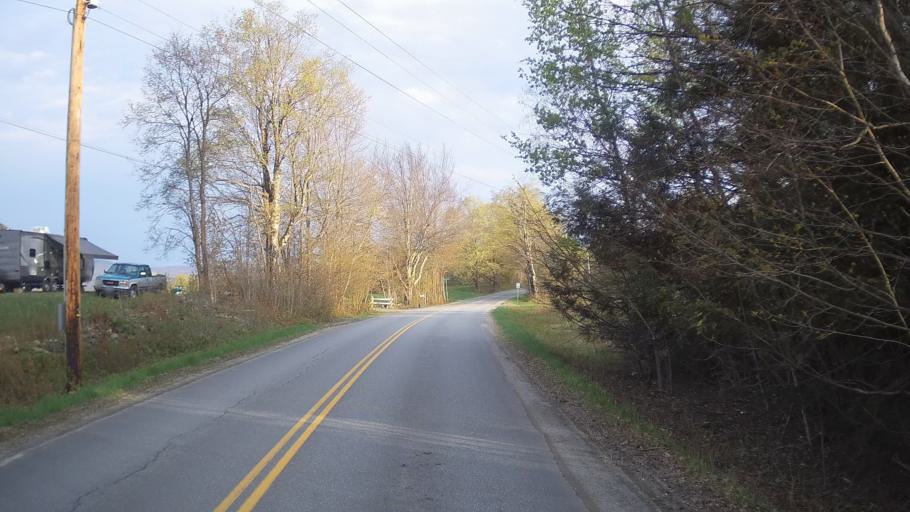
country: US
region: Vermont
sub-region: Orleans County
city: Newport
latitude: 44.9275
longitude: -72.4334
